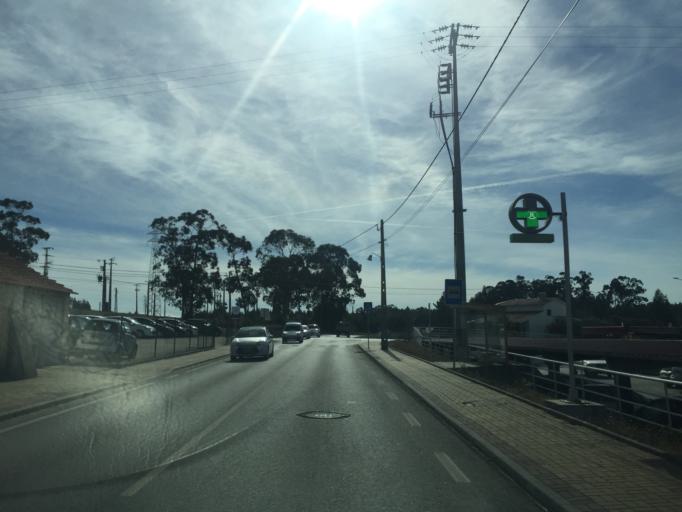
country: PT
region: Coimbra
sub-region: Figueira da Foz
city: Lavos
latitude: 40.0855
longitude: -8.8250
